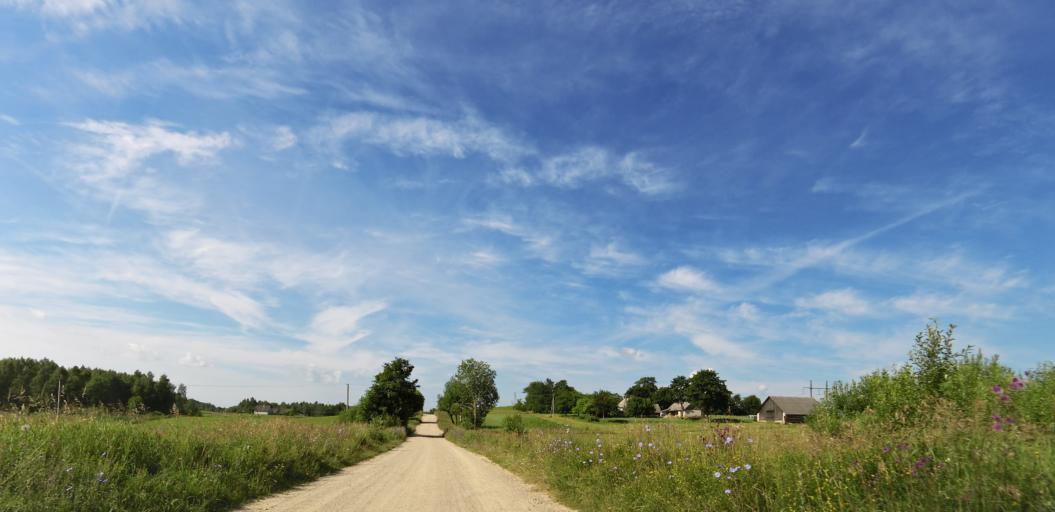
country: LT
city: Grigiskes
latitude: 54.7809
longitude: 25.0708
